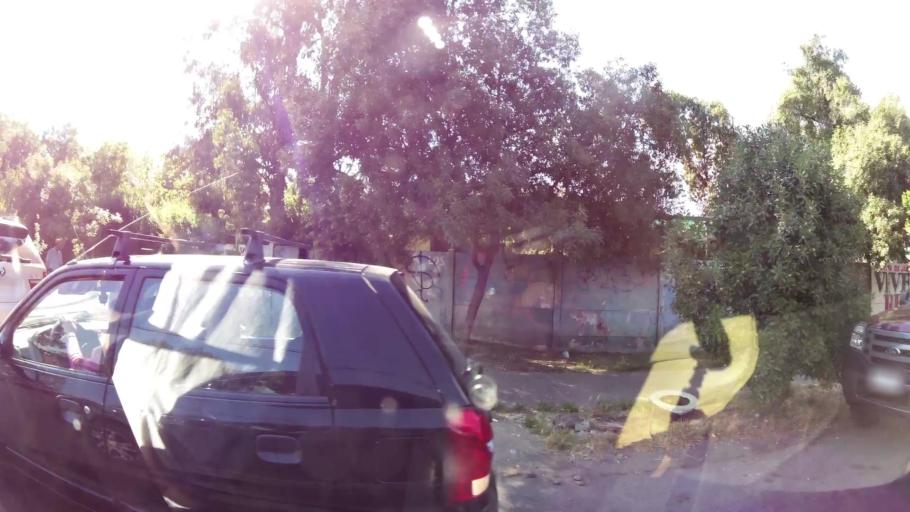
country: CL
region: Santiago Metropolitan
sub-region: Provincia de Maipo
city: San Bernardo
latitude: -33.5970
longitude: -70.6950
